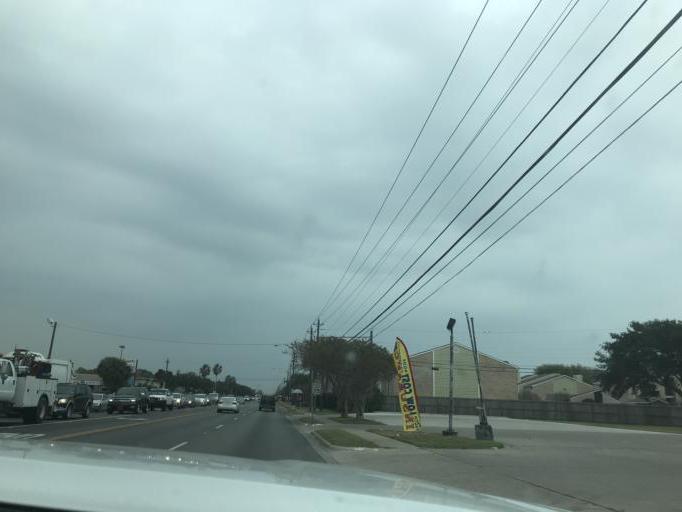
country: US
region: Texas
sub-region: Nueces County
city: Corpus Christi
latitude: 27.6923
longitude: -97.3633
